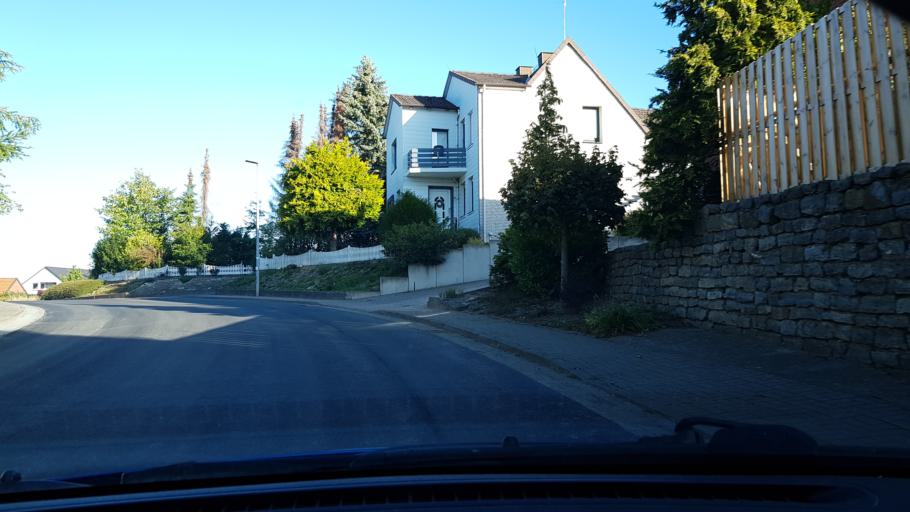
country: DE
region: Lower Saxony
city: Messenkamp
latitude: 52.2353
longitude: 9.4257
